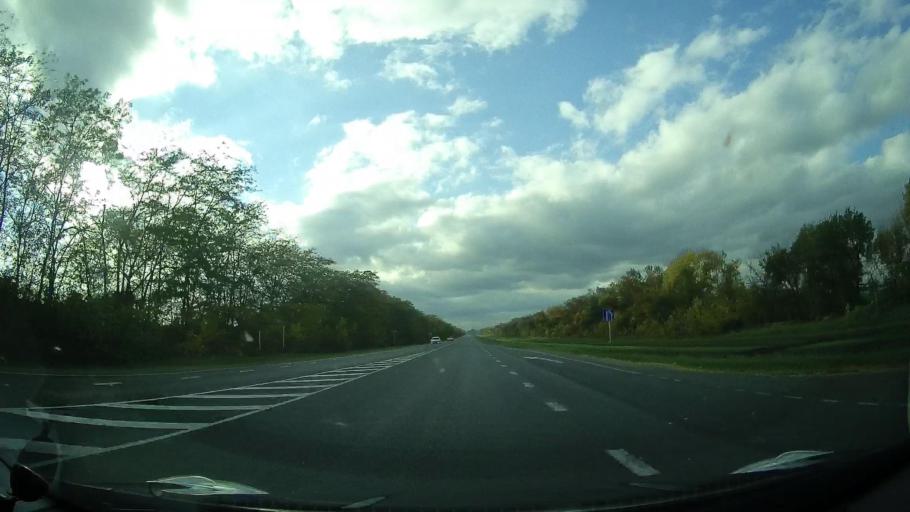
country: RU
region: Rostov
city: Kirovskaya
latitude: 47.0019
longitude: 39.9767
